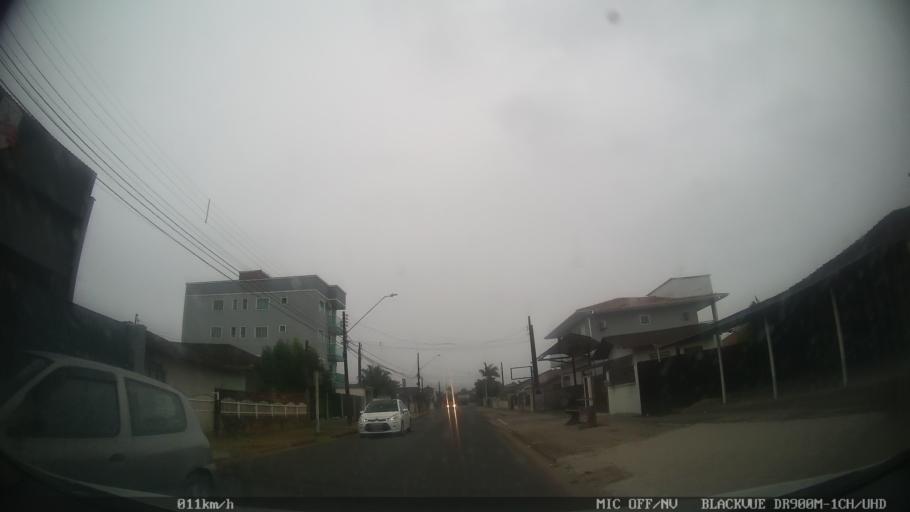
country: BR
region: Santa Catarina
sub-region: Joinville
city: Joinville
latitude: -26.2791
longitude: -48.8021
